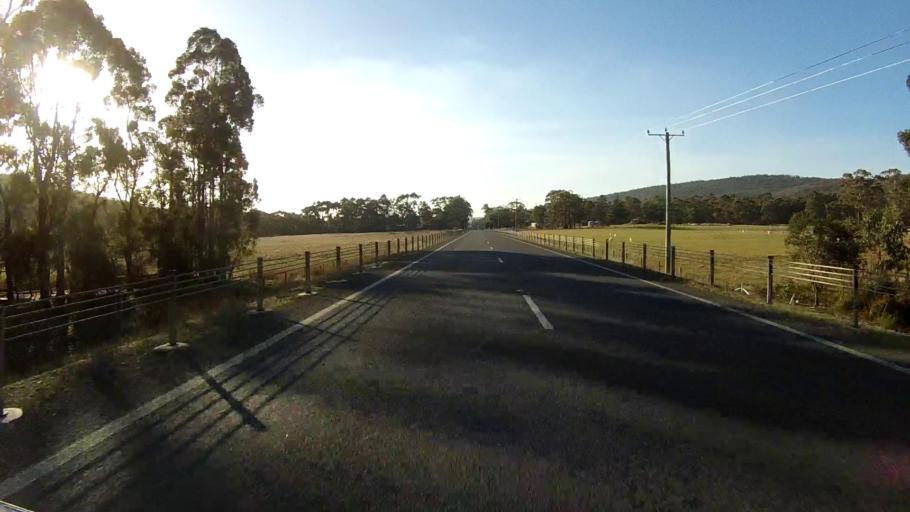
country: AU
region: Tasmania
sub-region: Clarence
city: Sandford
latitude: -43.0714
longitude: 147.8633
